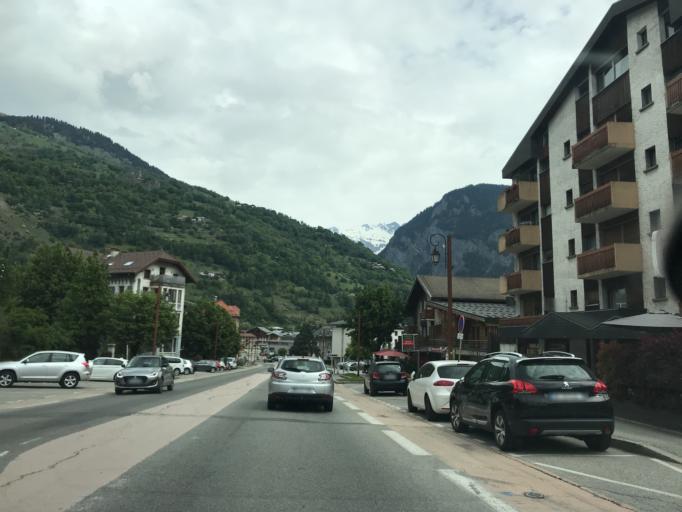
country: FR
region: Rhone-Alpes
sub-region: Departement de la Savoie
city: Bourg-Saint-Maurice
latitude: 45.6165
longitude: 6.7702
